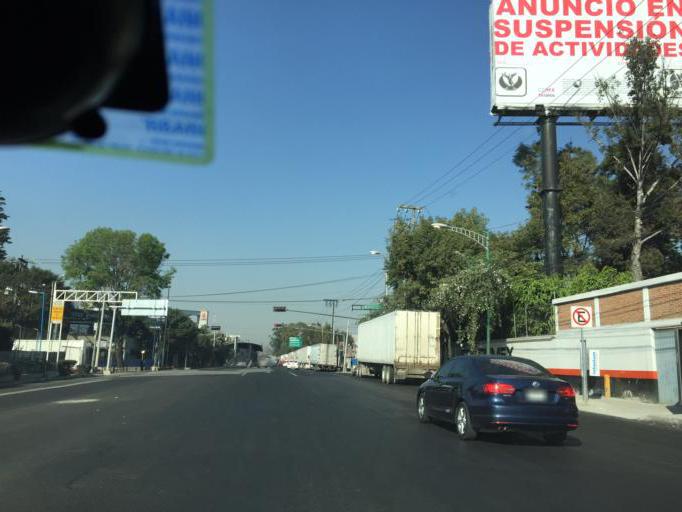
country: MX
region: Mexico City
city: Azcapotzalco
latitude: 19.4974
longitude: -99.1640
